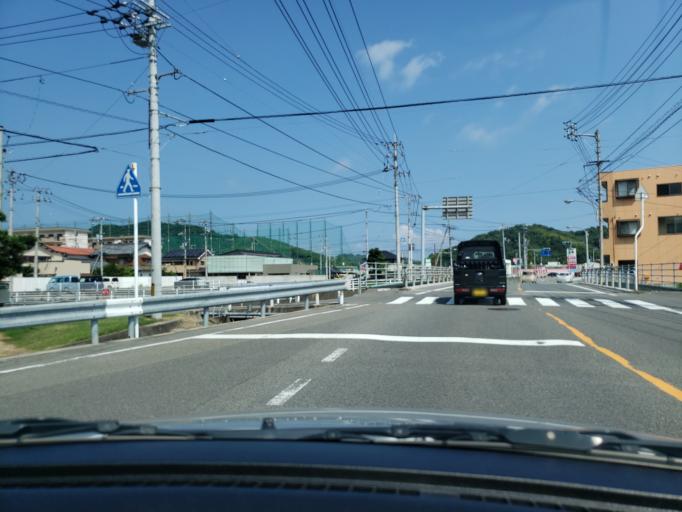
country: JP
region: Ehime
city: Hojo
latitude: 34.1008
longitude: 132.9680
